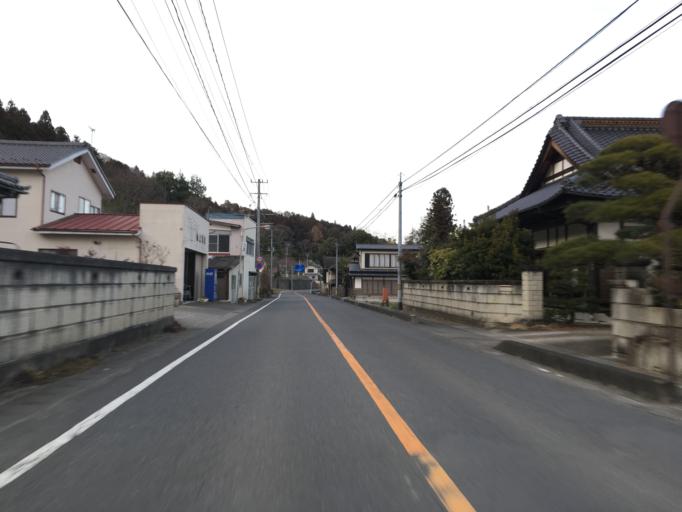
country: JP
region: Ibaraki
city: Daigo
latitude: 36.9025
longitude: 140.4066
